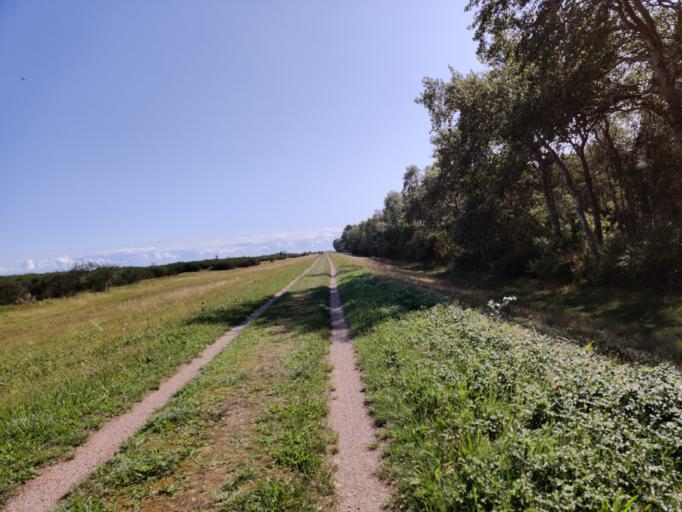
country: DK
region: Zealand
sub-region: Guldborgsund Kommune
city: Nykobing Falster
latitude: 54.6116
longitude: 11.9652
